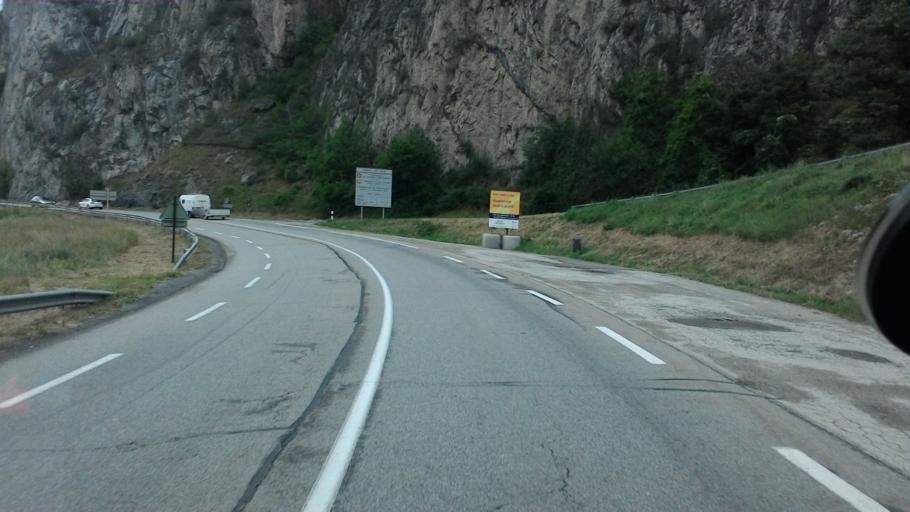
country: FR
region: Rhone-Alpes
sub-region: Departement de la Savoie
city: Aime
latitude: 45.5427
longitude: 6.6109
